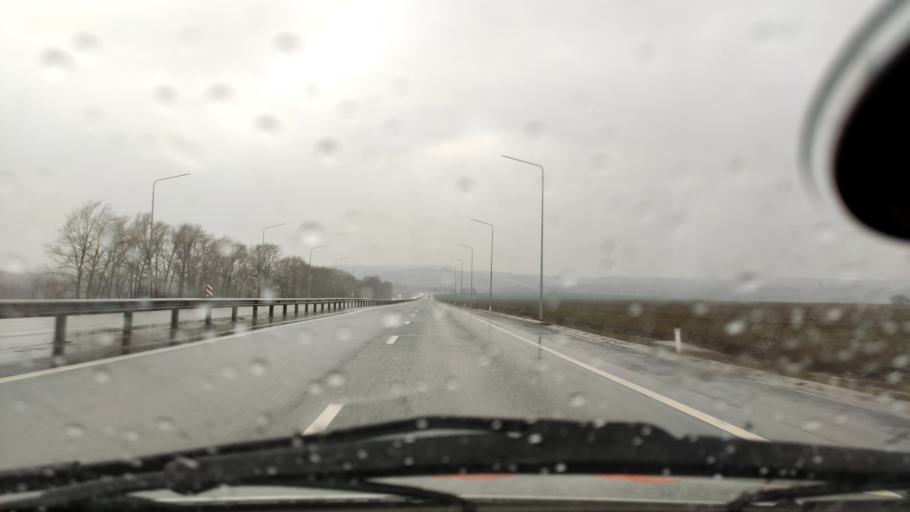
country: RU
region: Bashkortostan
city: Tolbazy
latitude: 54.0477
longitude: 55.8875
